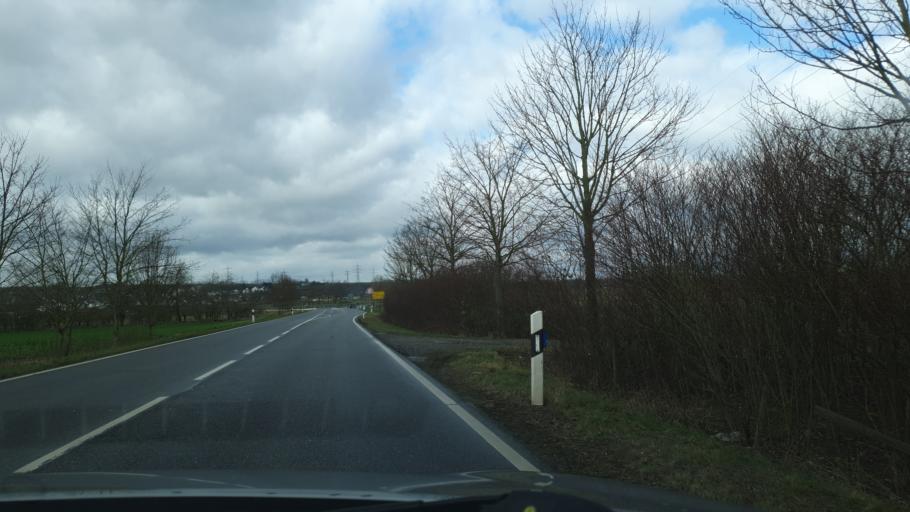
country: DE
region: Rheinland-Pfalz
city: Mulheim-Karlich
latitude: 50.3953
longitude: 7.4853
